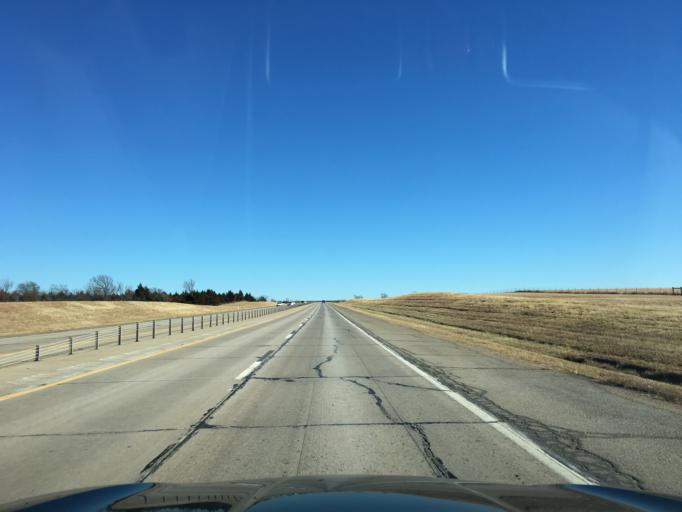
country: US
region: Oklahoma
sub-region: Pawnee County
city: Pawnee
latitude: 36.2251
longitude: -96.8483
